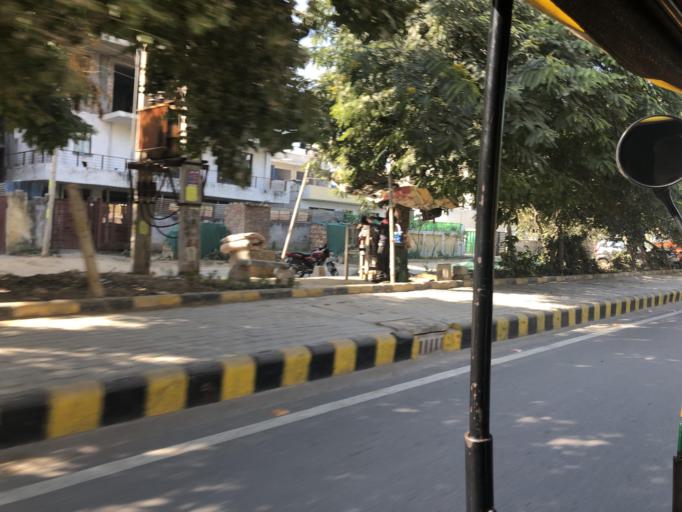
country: IN
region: Haryana
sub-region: Gurgaon
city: Gurgaon
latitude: 28.4514
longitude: 77.0678
